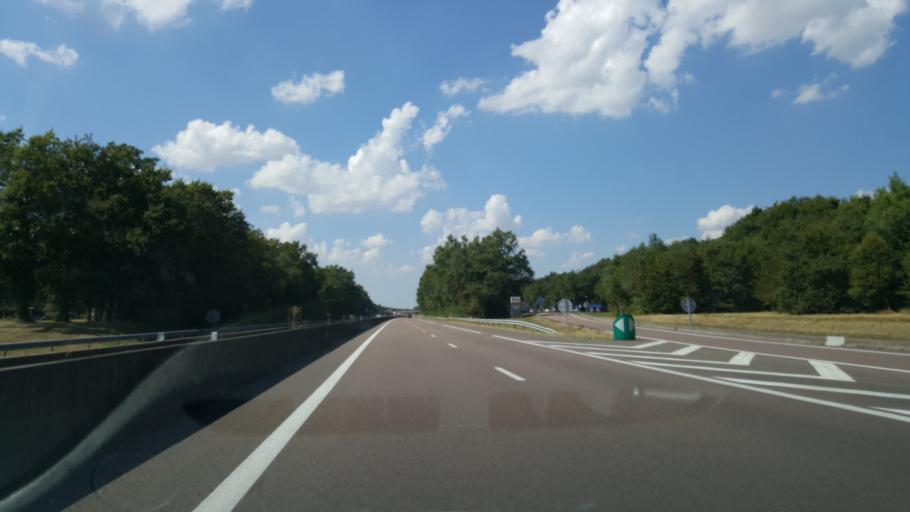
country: FR
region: Bourgogne
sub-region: Departement de la Cote-d'Or
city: Semur-en-Auxois
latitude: 47.3876
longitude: 4.3674
